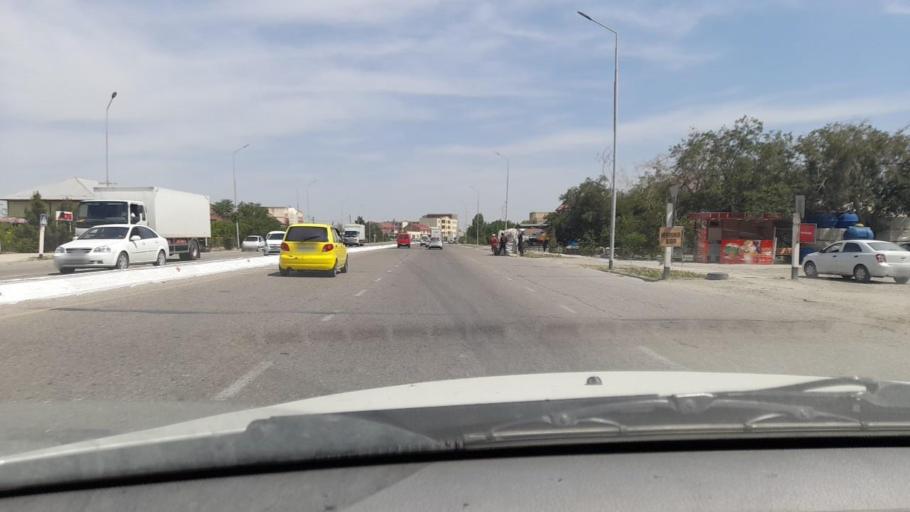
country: UZ
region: Bukhara
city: Galaosiyo
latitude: 39.8598
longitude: 64.4434
